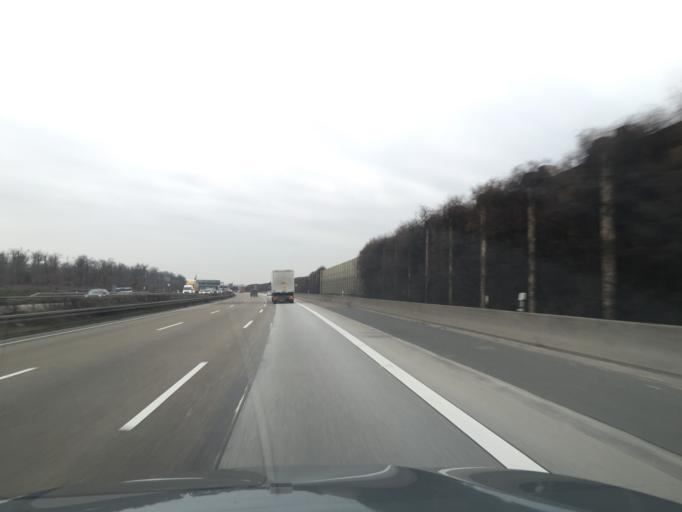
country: DE
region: Hesse
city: Kelsterbach
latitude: 50.0479
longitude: 8.5473
